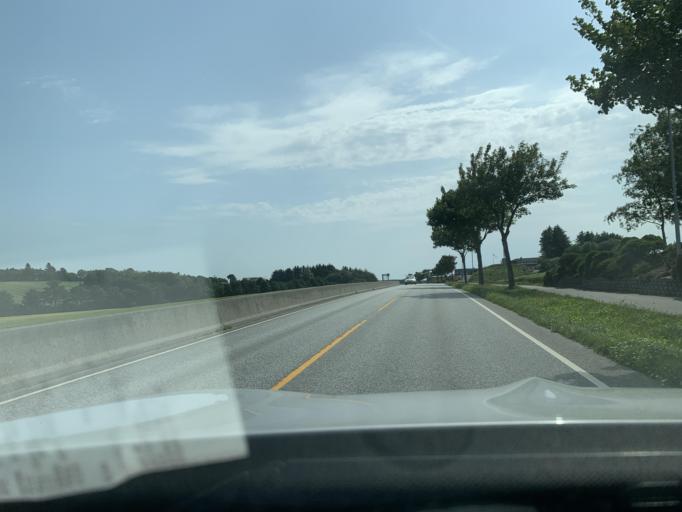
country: NO
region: Rogaland
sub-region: Klepp
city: Kleppe
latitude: 58.7640
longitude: 5.6255
